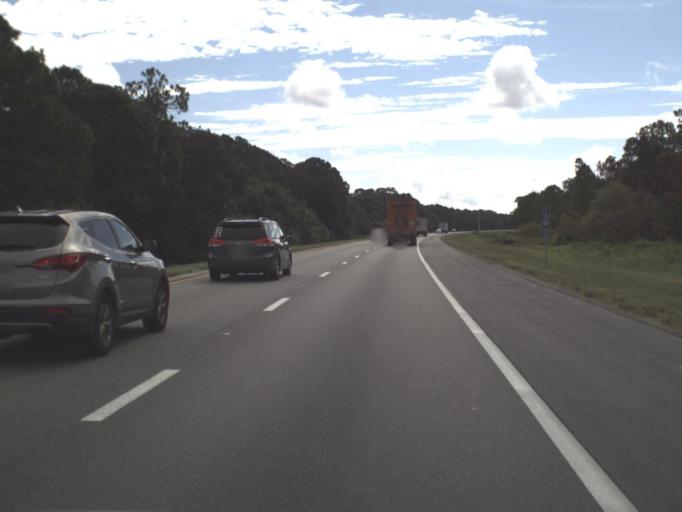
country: US
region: Florida
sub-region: Sarasota County
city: Plantation
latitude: 27.1121
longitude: -82.3223
